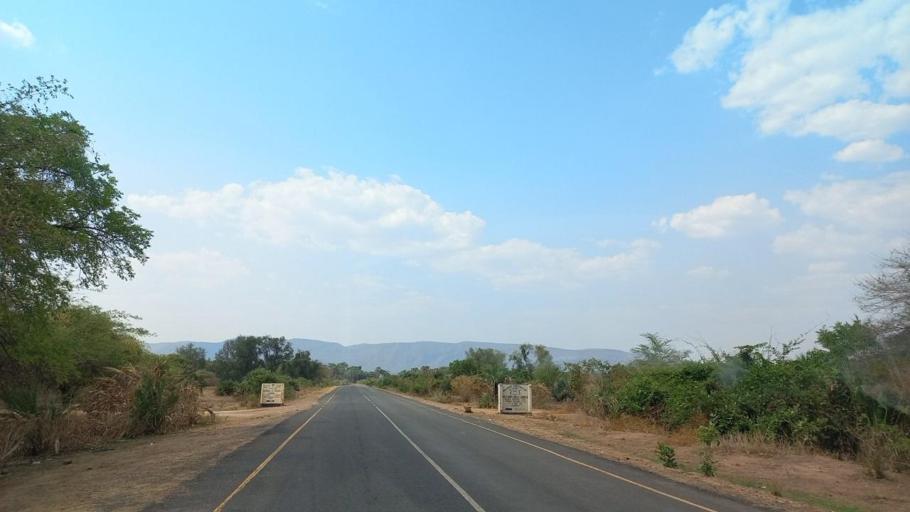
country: ZM
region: Lusaka
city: Luangwa
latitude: -15.0961
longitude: 30.1930
